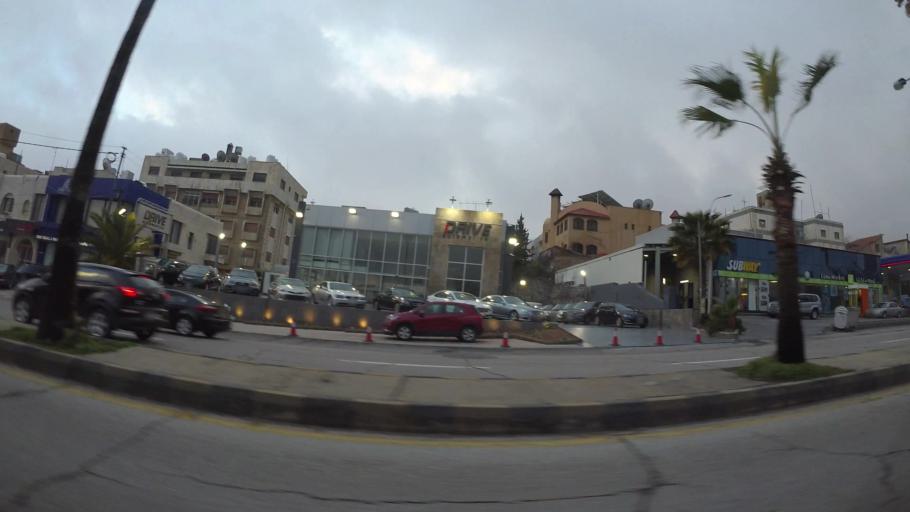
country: JO
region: Amman
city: Al Jubayhah
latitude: 31.9655
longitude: 35.8827
